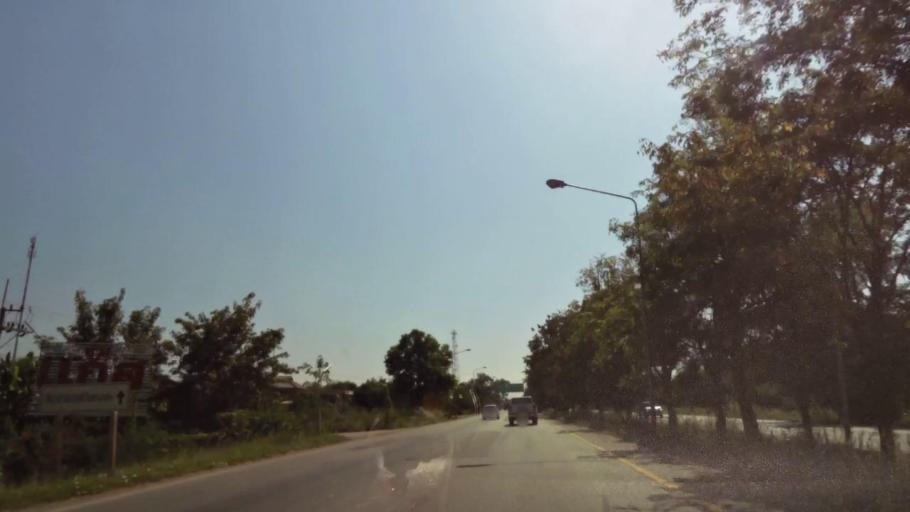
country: TH
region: Nakhon Sawan
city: Kao Liao
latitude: 15.8739
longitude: 100.1163
